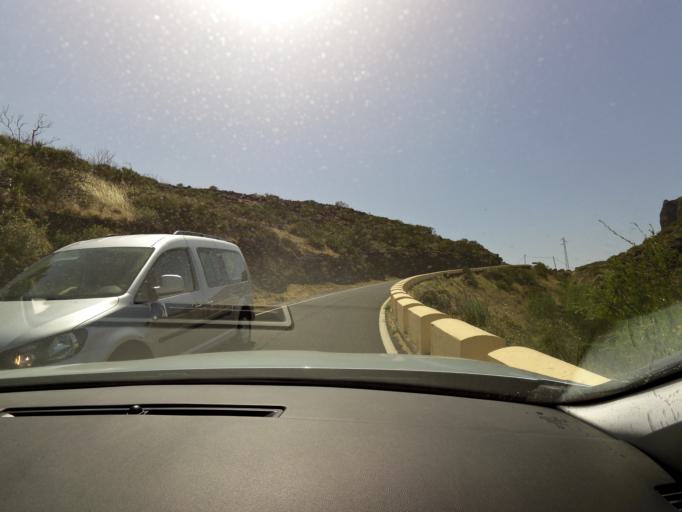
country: ES
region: Canary Islands
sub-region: Provincia de Santa Cruz de Tenerife
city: Santiago del Teide
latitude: 28.2989
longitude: -16.8228
